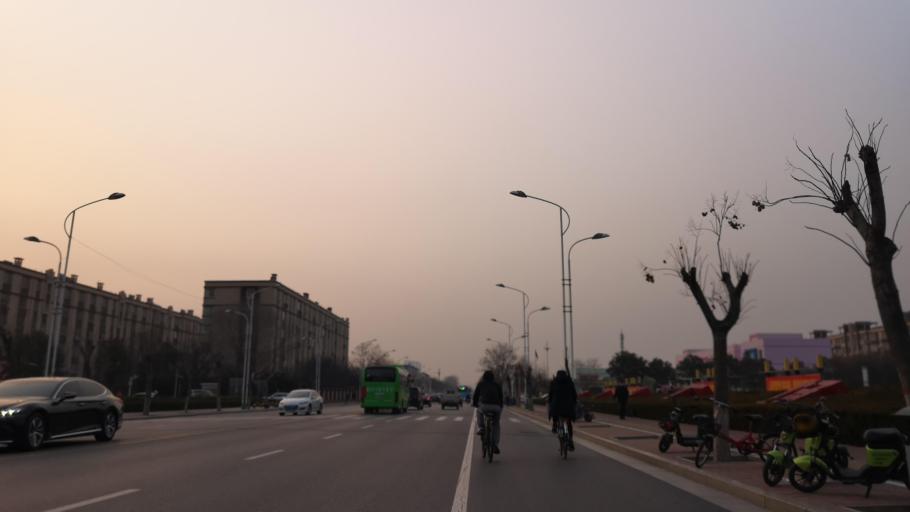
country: CN
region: Henan Sheng
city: Zhongyuanlu
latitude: 35.7838
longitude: 115.0798
